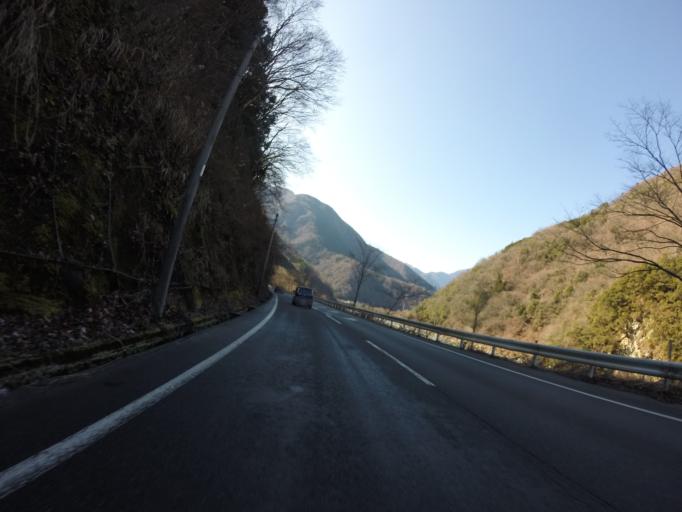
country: JP
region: Yamanashi
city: Ryuo
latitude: 35.4152
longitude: 138.3781
